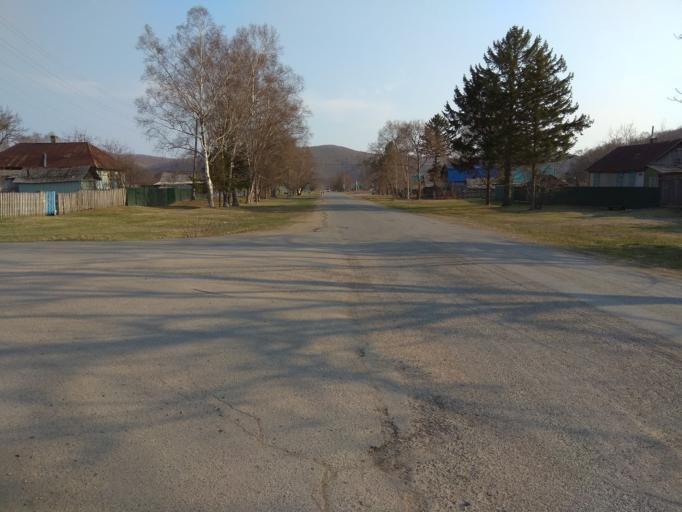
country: RU
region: Primorskiy
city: Lazo
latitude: 43.3101
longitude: 134.6040
